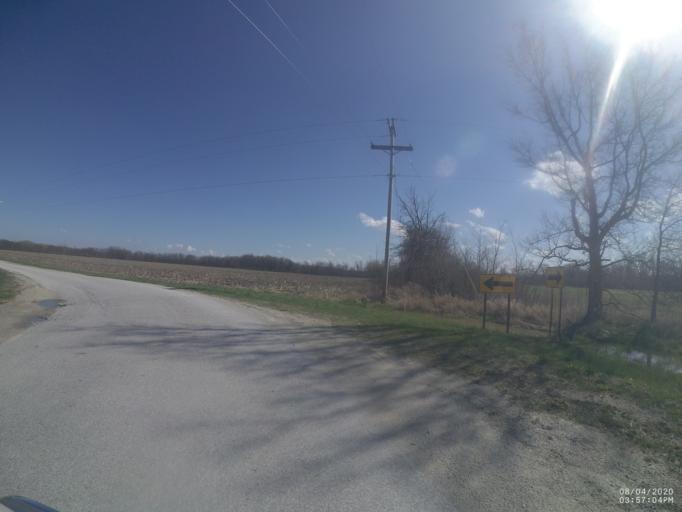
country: US
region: Ohio
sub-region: Sandusky County
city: Ballville
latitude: 41.2724
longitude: -83.1972
